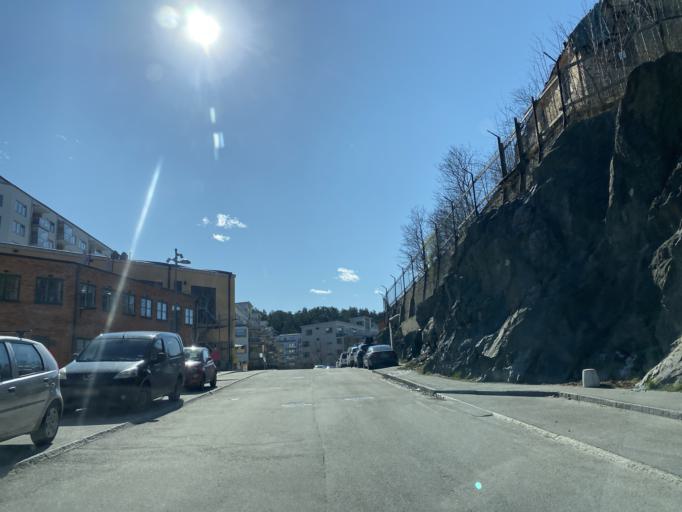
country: SE
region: Stockholm
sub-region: Nacka Kommun
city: Nacka
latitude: 59.3154
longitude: 18.1240
